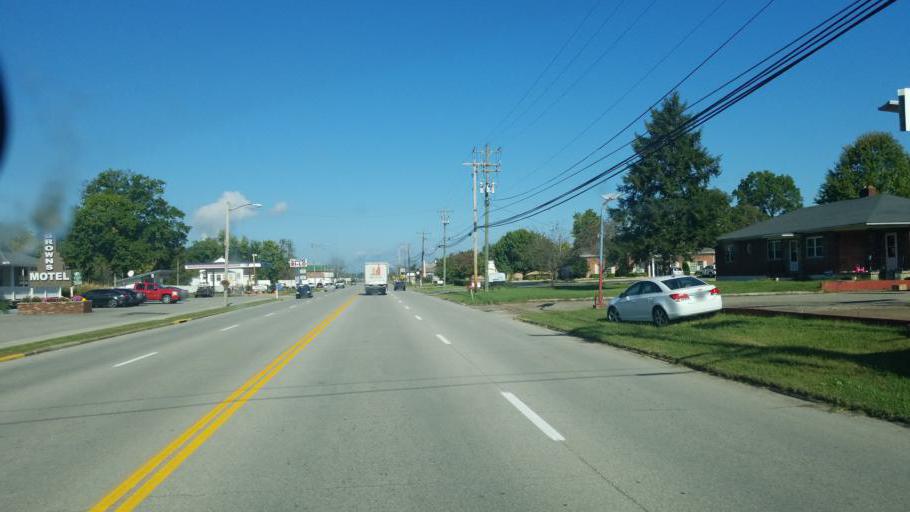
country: US
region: Ohio
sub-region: Brown County
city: Aberdeen
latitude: 38.6584
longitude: -83.7655
